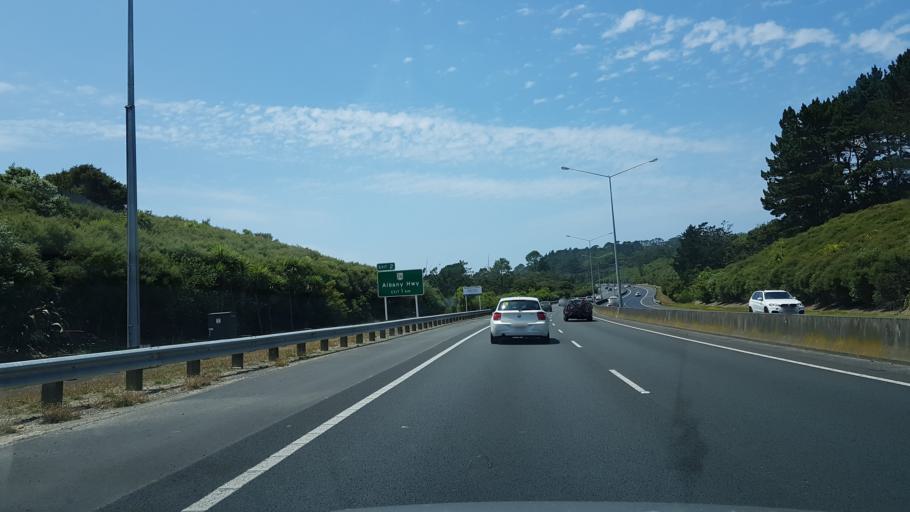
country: NZ
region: Auckland
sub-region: Auckland
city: Rothesay Bay
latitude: -36.7657
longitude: 174.6908
